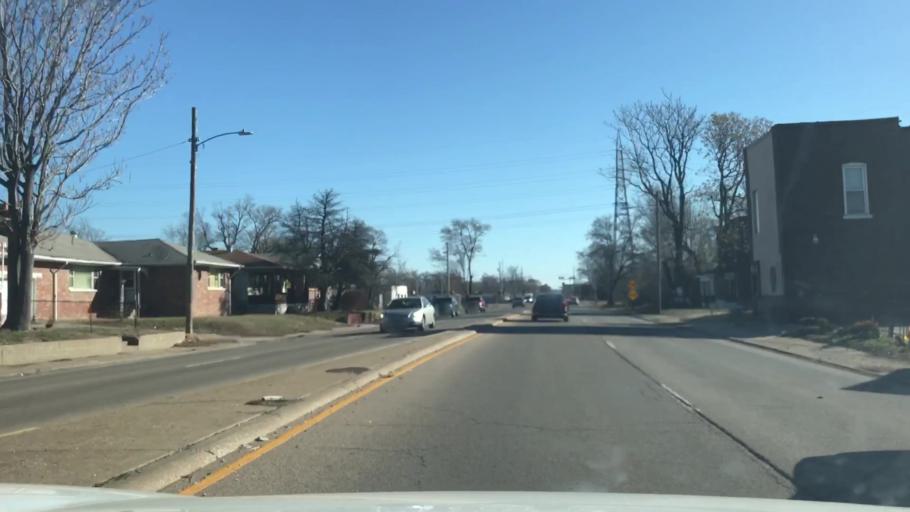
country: US
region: Illinois
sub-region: Saint Clair County
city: East Saint Louis
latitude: 38.6123
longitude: -90.1426
